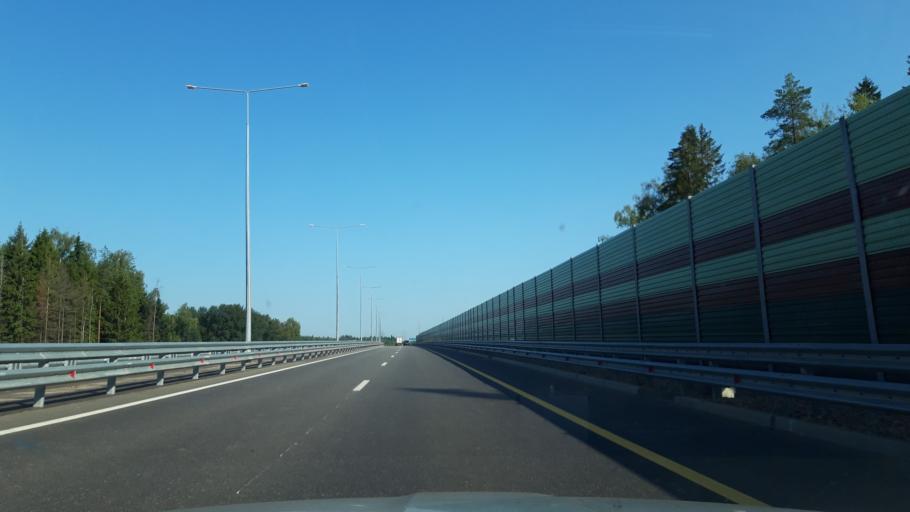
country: RU
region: Moskovskaya
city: Spas-Zaulok
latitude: 56.4904
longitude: 36.5327
